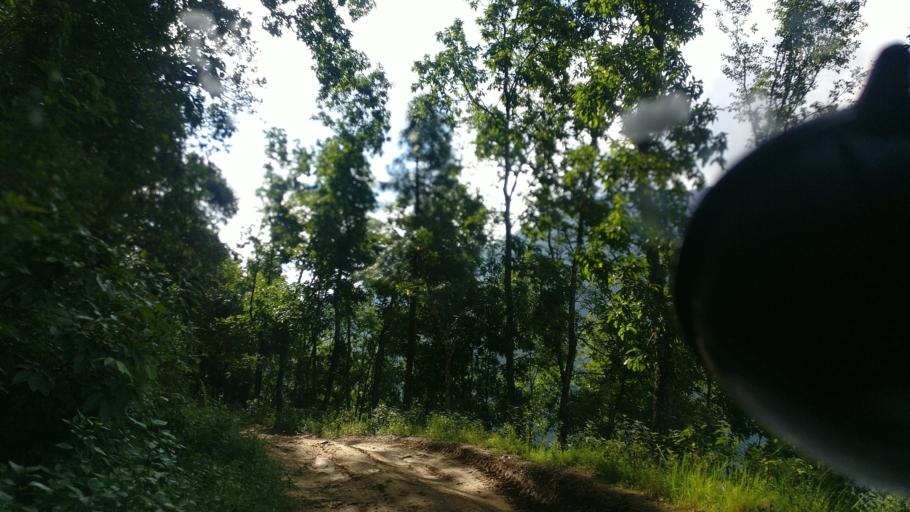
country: NP
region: Western Region
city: Baglung
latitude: 28.1364
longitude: 83.6542
